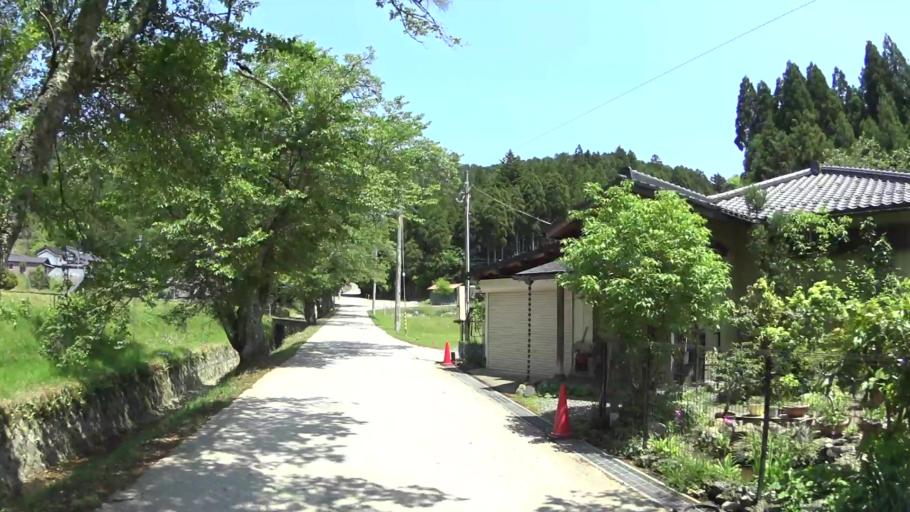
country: JP
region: Kyoto
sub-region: Kyoto-shi
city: Kamigyo-ku
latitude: 35.1986
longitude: 135.6813
